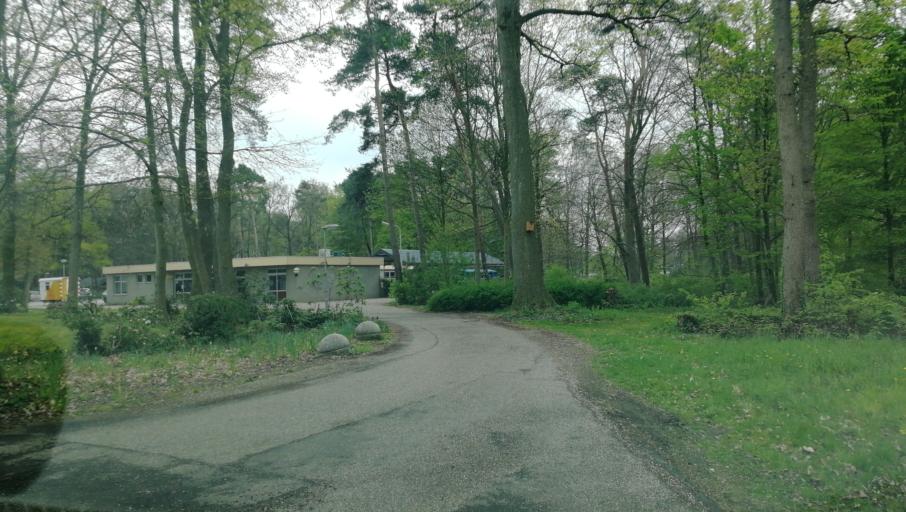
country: NL
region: Limburg
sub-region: Gemeente Venlo
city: Venlo
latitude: 51.3686
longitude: 6.1947
